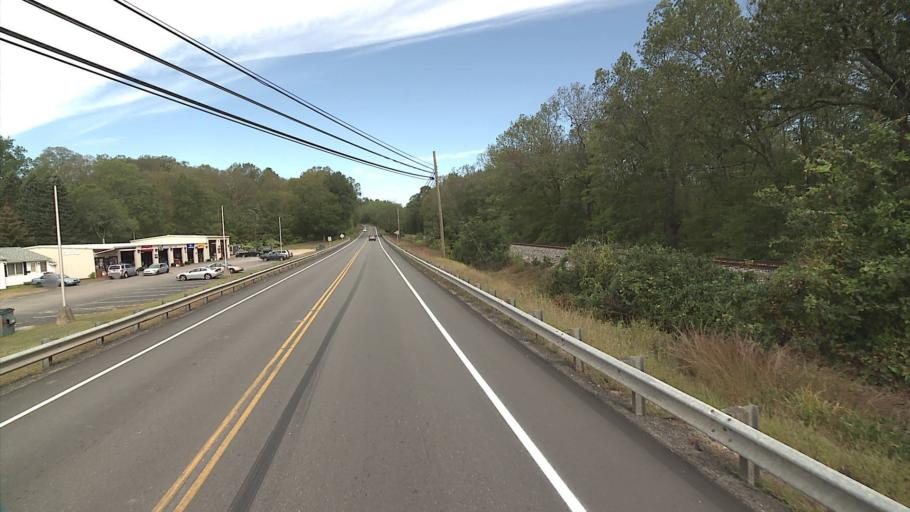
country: US
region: Connecticut
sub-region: Windham County
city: South Windham
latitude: 41.6932
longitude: -72.1809
